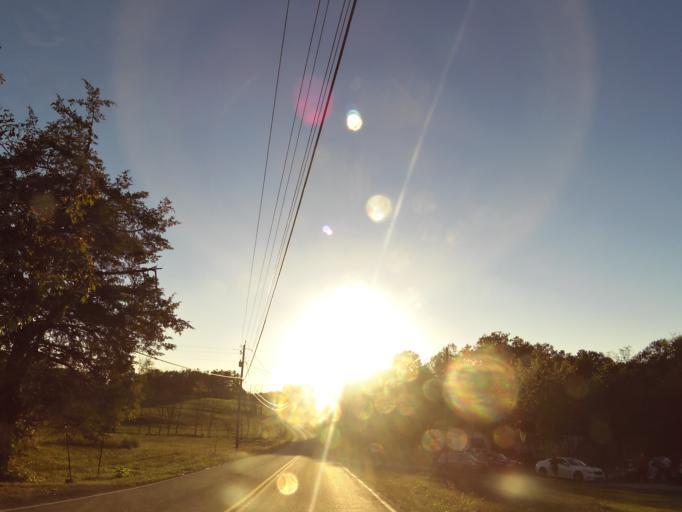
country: US
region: Tennessee
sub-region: Grainger County
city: Rutledge
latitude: 36.2846
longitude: -83.6102
